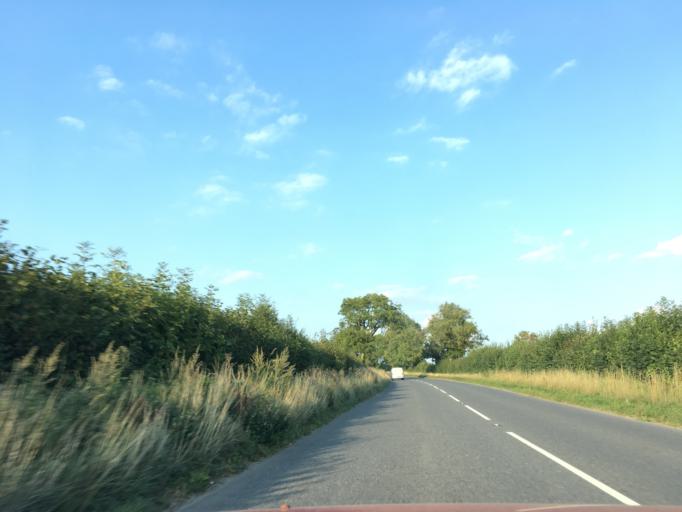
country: GB
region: England
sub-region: Gloucestershire
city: Stow on the Wold
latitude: 51.9119
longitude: -1.7318
